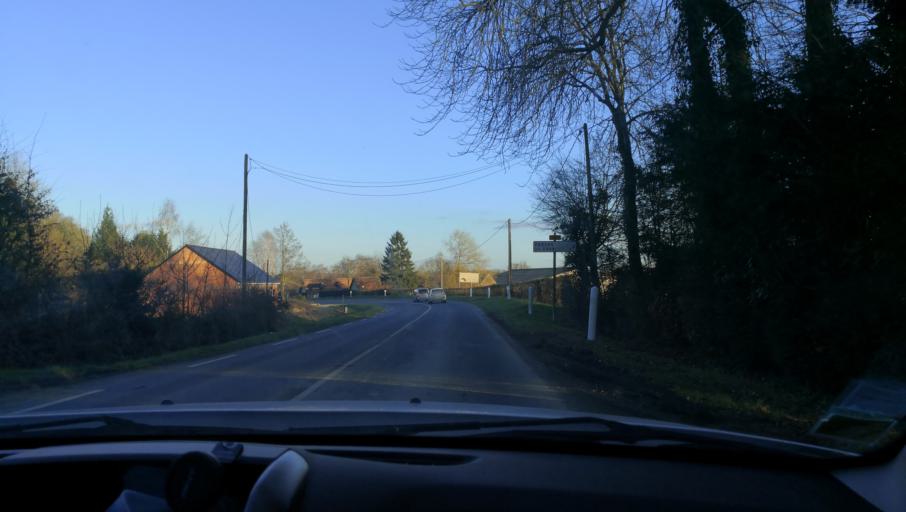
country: FR
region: Haute-Normandie
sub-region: Departement de la Seine-Maritime
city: Forges-les-Eaux
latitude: 49.6084
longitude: 1.5162
